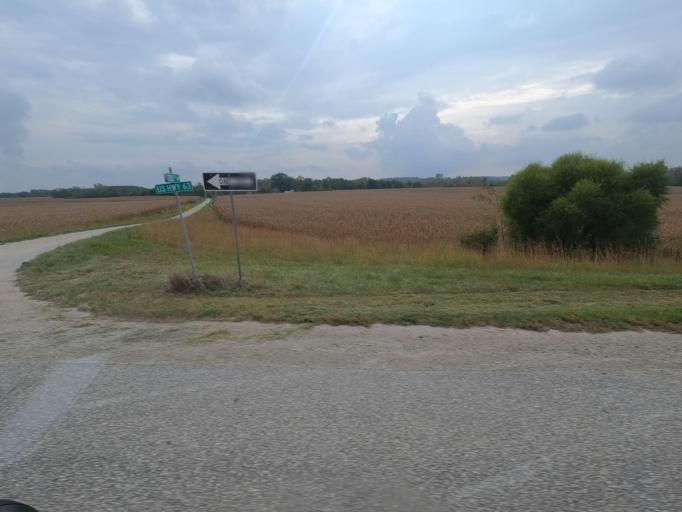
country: US
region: Iowa
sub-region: Wapello County
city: Eddyville
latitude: 41.1353
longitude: -92.5829
